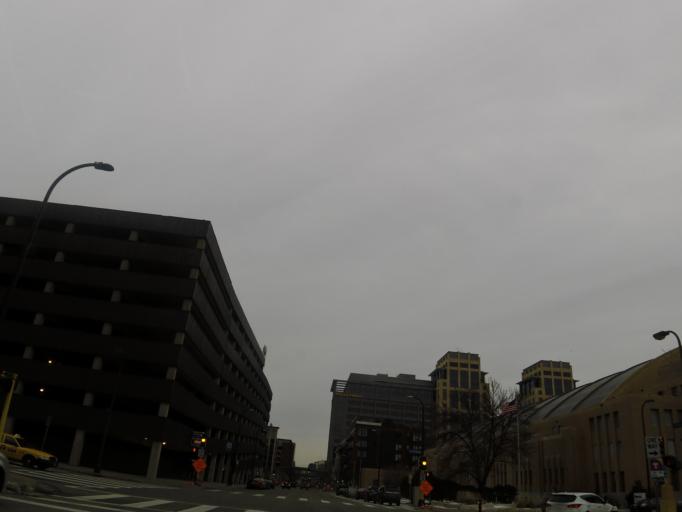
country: US
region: Minnesota
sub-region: Hennepin County
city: Minneapolis
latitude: 44.9747
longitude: -93.2649
